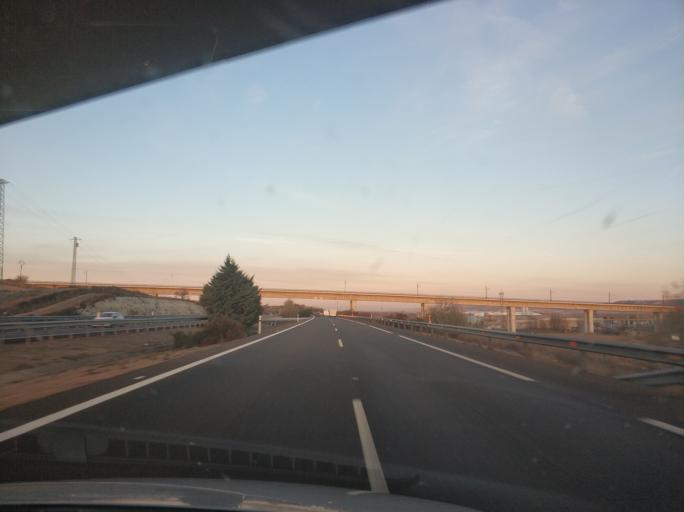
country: ES
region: Castille and Leon
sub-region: Provincia de Palencia
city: Venta de Banos
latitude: 41.9481
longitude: -4.4698
